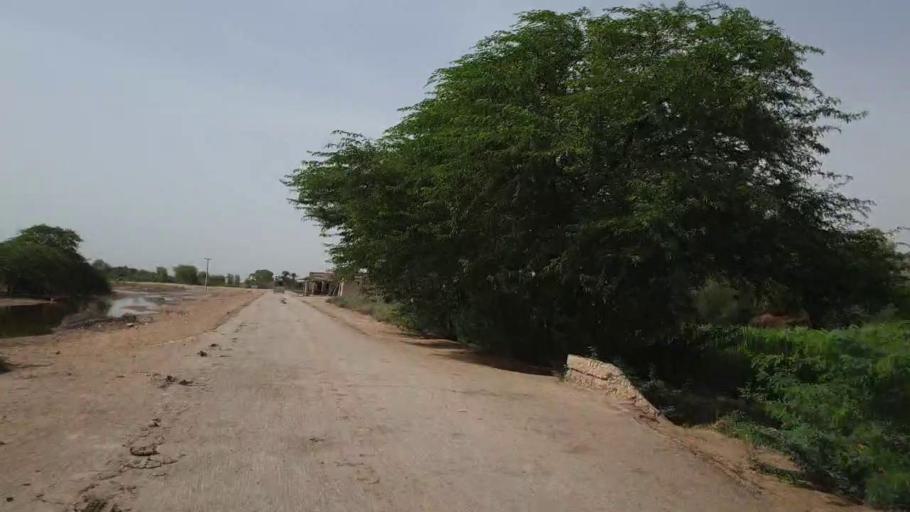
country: PK
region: Sindh
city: Bandhi
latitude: 26.5687
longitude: 68.3805
